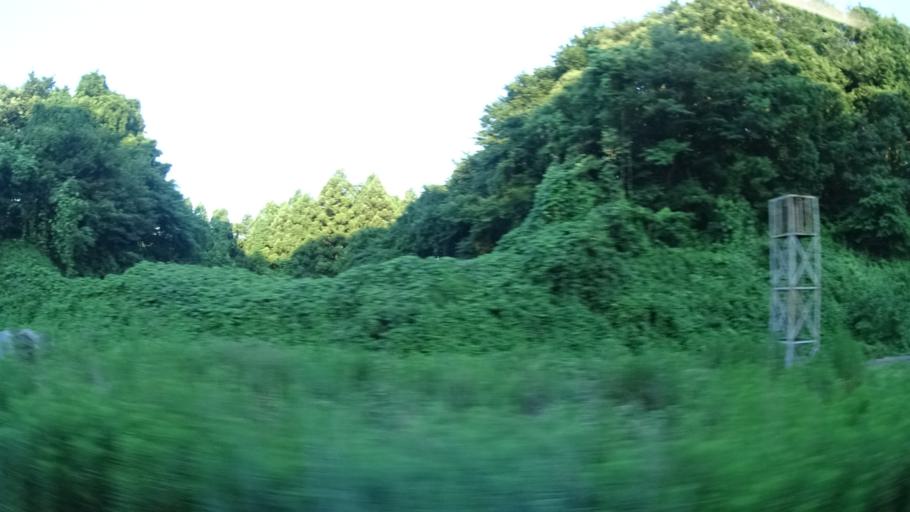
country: JP
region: Ibaraki
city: Naka
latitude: 36.0577
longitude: 140.1867
